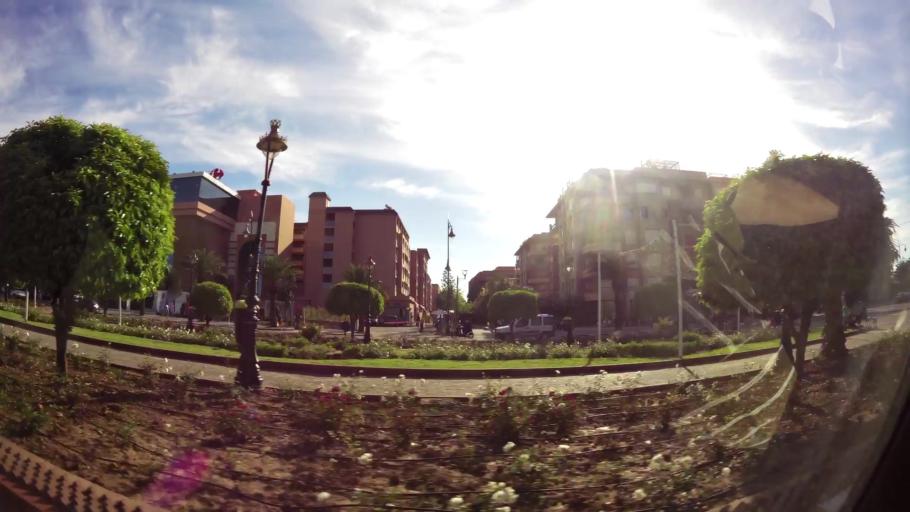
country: MA
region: Marrakech-Tensift-Al Haouz
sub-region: Marrakech
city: Marrakesh
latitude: 31.6198
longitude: -8.0092
